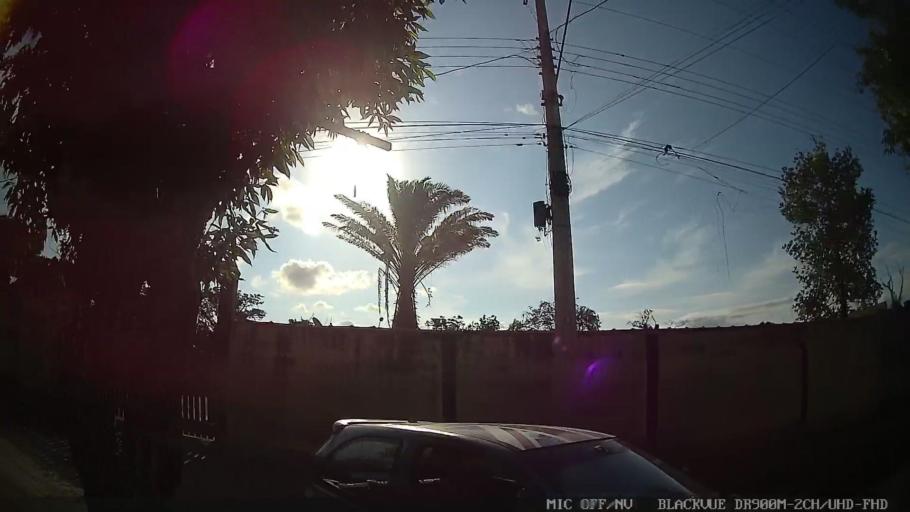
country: BR
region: Sao Paulo
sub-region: Itanhaem
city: Itanhaem
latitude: -24.1705
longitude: -46.8183
